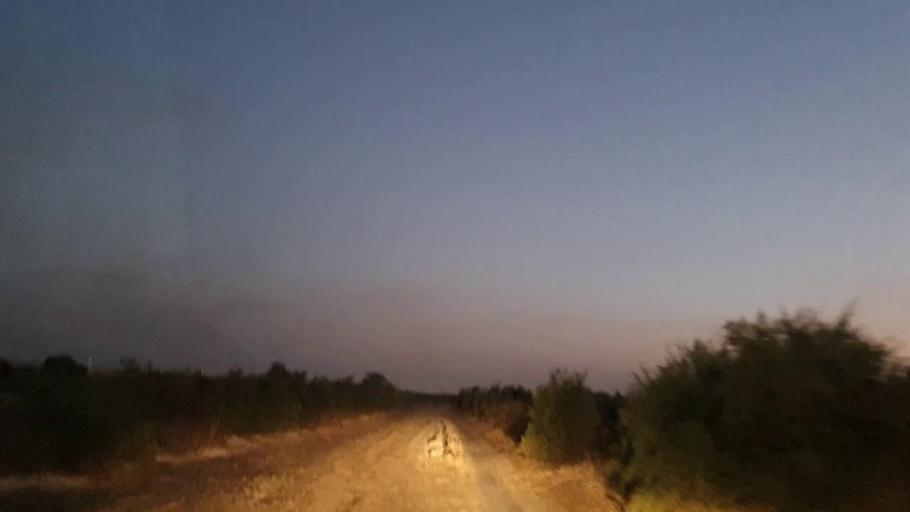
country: PK
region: Sindh
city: Nawabshah
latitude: 26.3306
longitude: 68.3752
